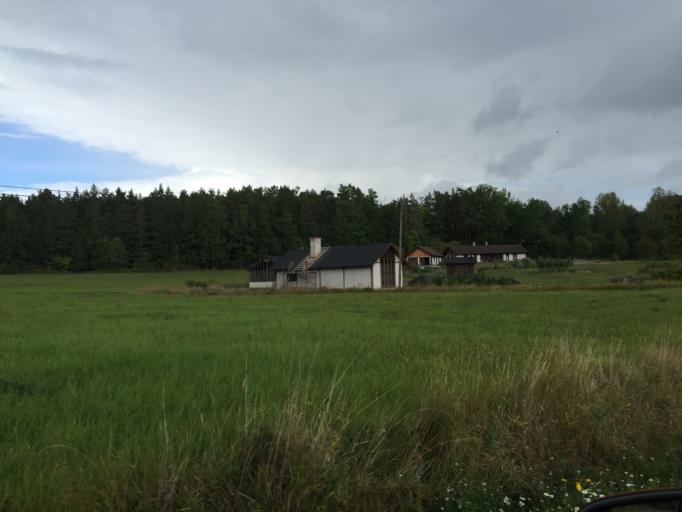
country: SE
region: Kalmar
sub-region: Vasterviks Kommun
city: Gamleby
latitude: 57.7902
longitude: 16.4435
